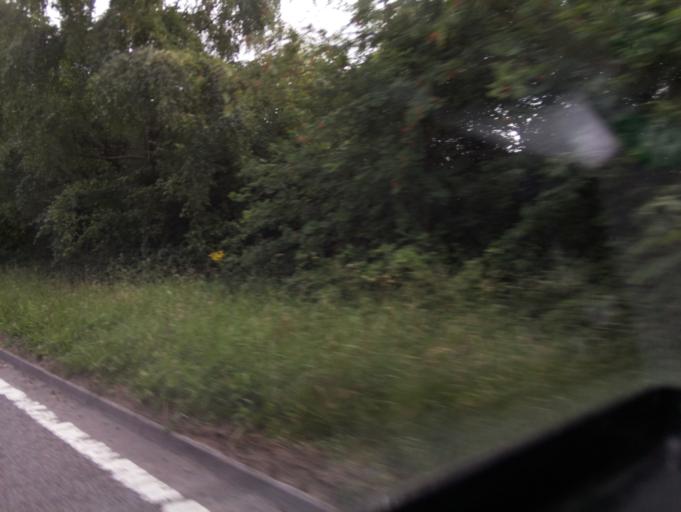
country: GB
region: Wales
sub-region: Monmouthshire
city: Chepstow
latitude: 51.6506
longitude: -2.6571
